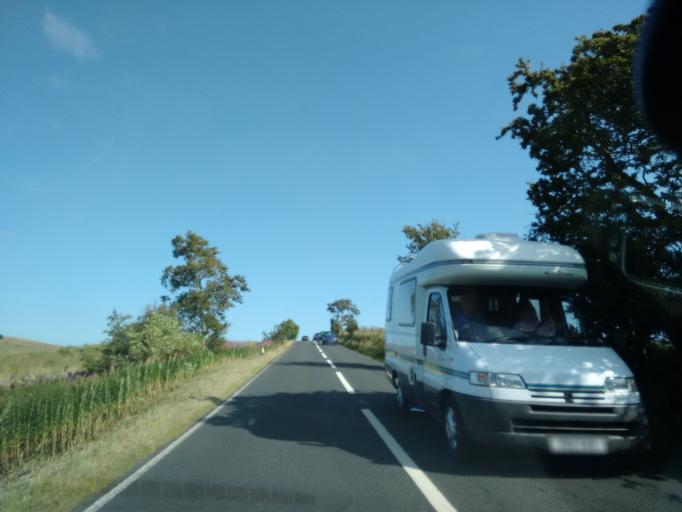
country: GB
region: England
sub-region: Northumberland
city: Bardon Mill
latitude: 54.9988
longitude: -2.3716
